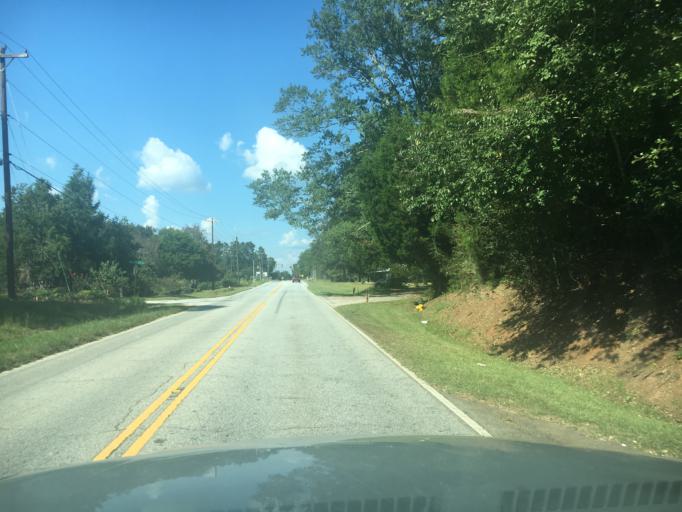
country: US
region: South Carolina
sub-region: Greenwood County
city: Greenwood
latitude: 34.2455
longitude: -82.1807
